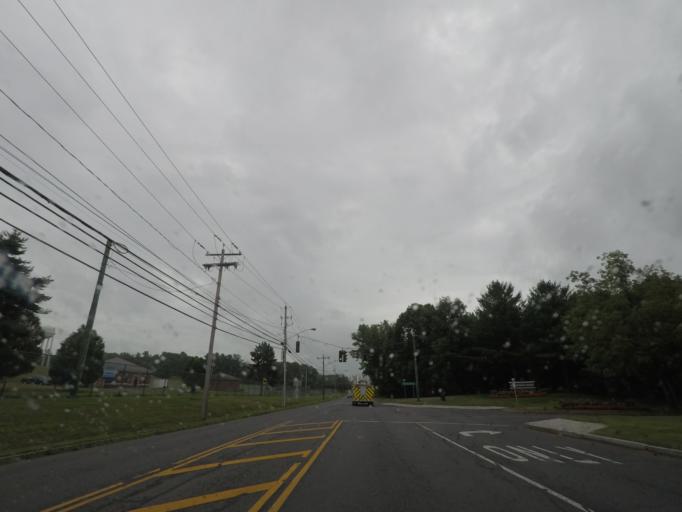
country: US
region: New York
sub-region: Albany County
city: West Albany
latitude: 42.6821
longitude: -73.7590
